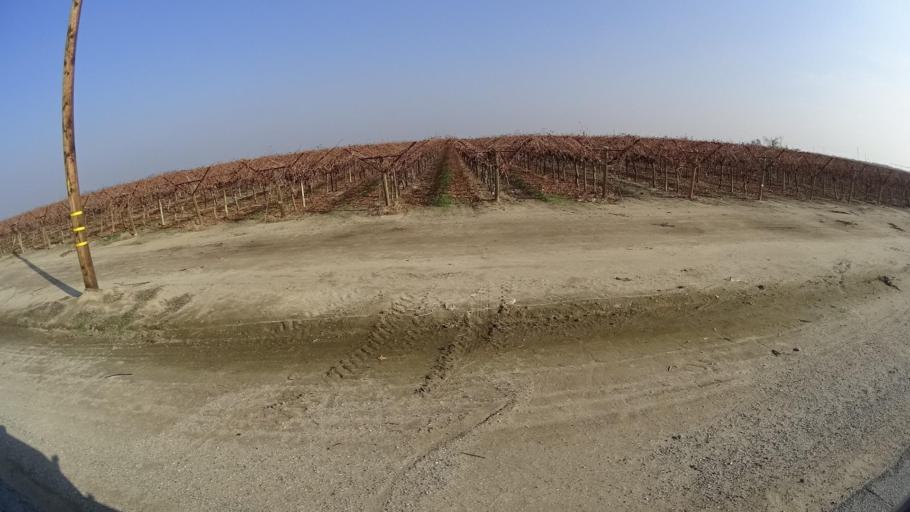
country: US
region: California
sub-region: Kern County
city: Greenfield
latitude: 35.2141
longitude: -119.0392
